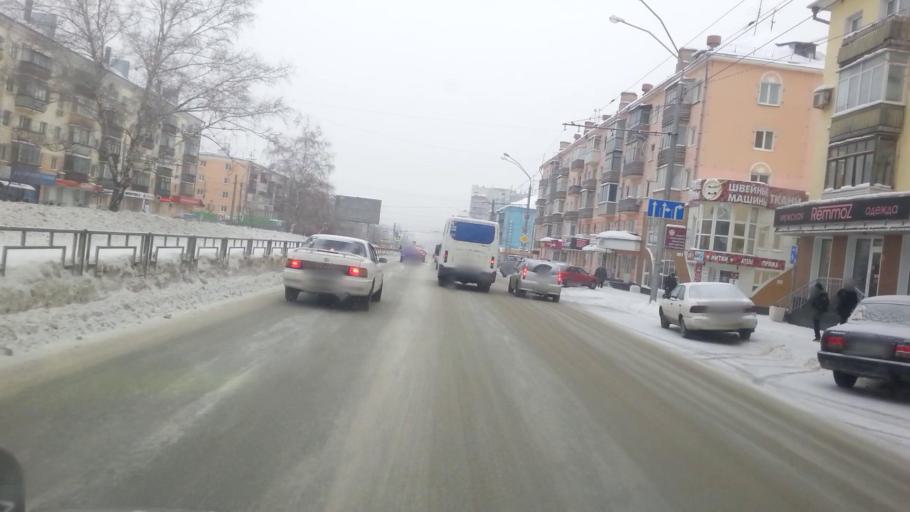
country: RU
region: Altai Krai
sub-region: Gorod Barnaulskiy
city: Barnaul
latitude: 53.3741
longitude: 83.7482
